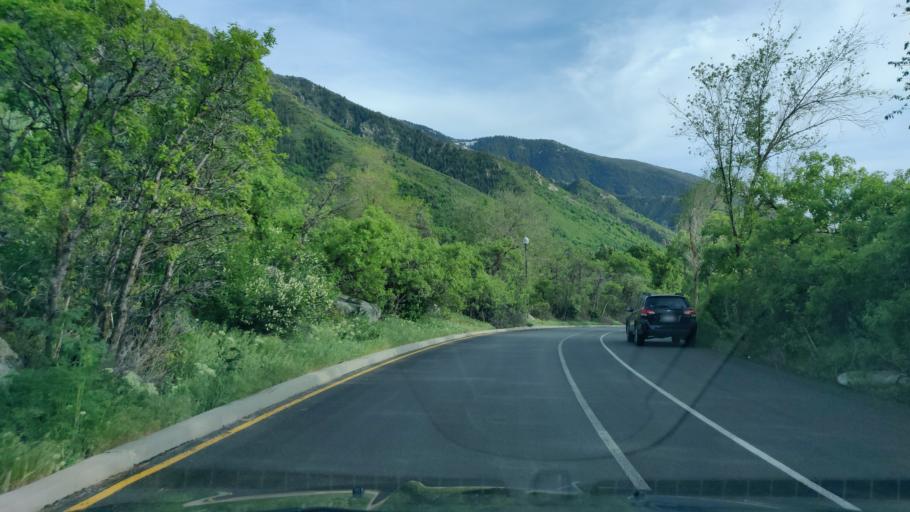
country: US
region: Utah
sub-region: Salt Lake County
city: Granite
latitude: 40.5587
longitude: -111.8000
